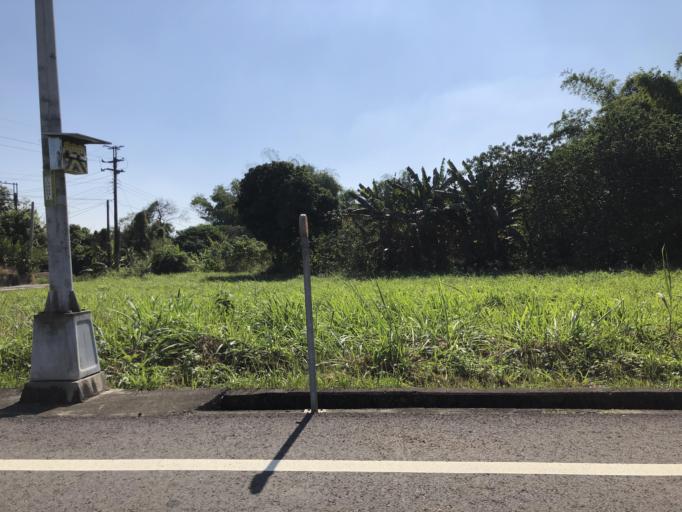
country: TW
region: Taiwan
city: Yujing
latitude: 23.0644
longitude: 120.3846
